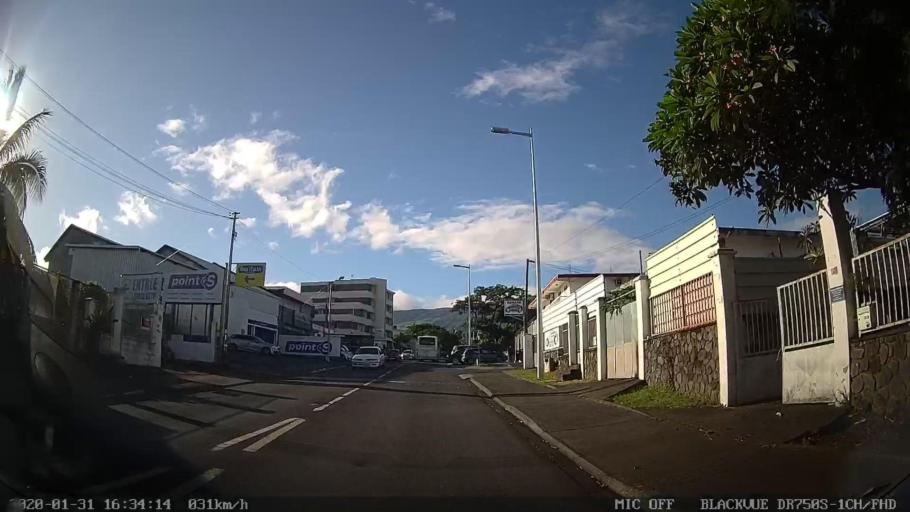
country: RE
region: Reunion
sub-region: Reunion
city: Saint-Denis
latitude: -20.8987
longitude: 55.4917
